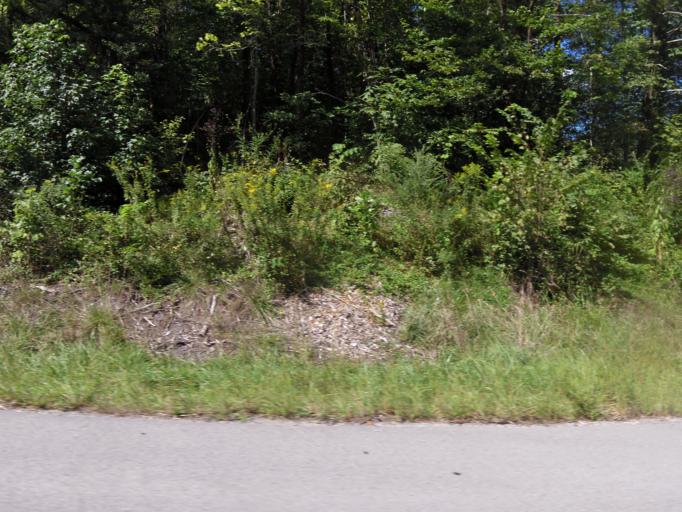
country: US
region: Kentucky
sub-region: Bell County
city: Pineville
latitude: 36.7943
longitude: -83.5378
